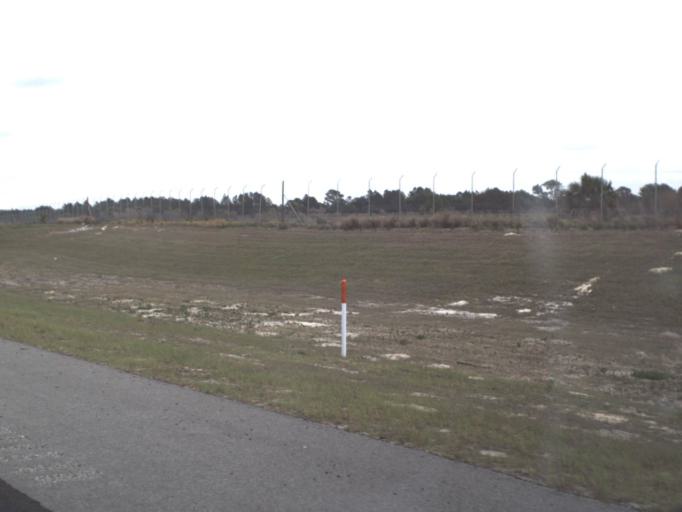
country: US
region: Florida
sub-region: Lake County
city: Mount Plymouth
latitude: 28.8046
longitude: -81.5132
